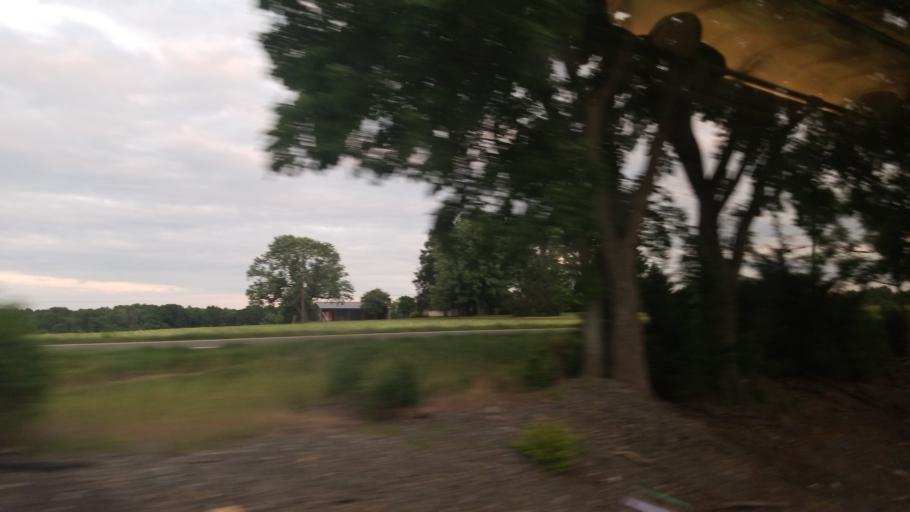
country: US
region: Virginia
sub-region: Culpeper County
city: Culpeper
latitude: 38.4256
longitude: -78.0006
